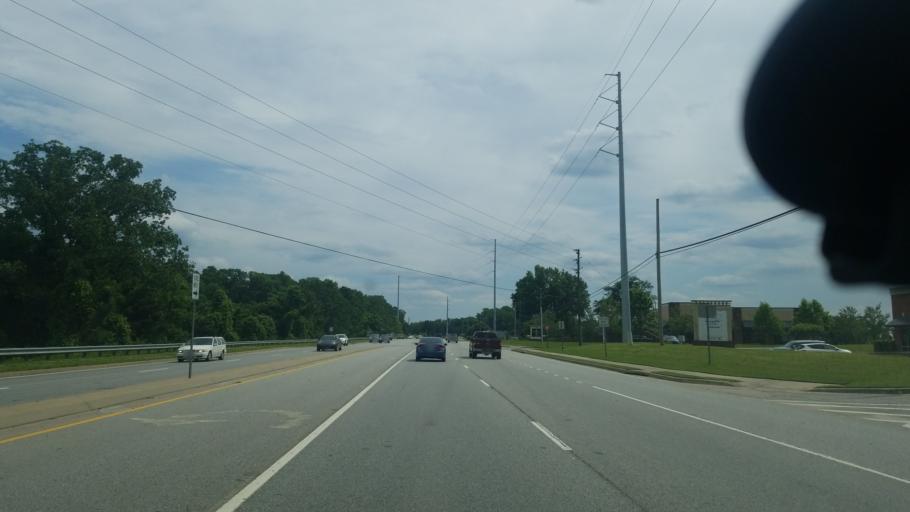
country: US
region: Georgia
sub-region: Forsyth County
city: Cumming
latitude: 34.1616
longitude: -84.1530
